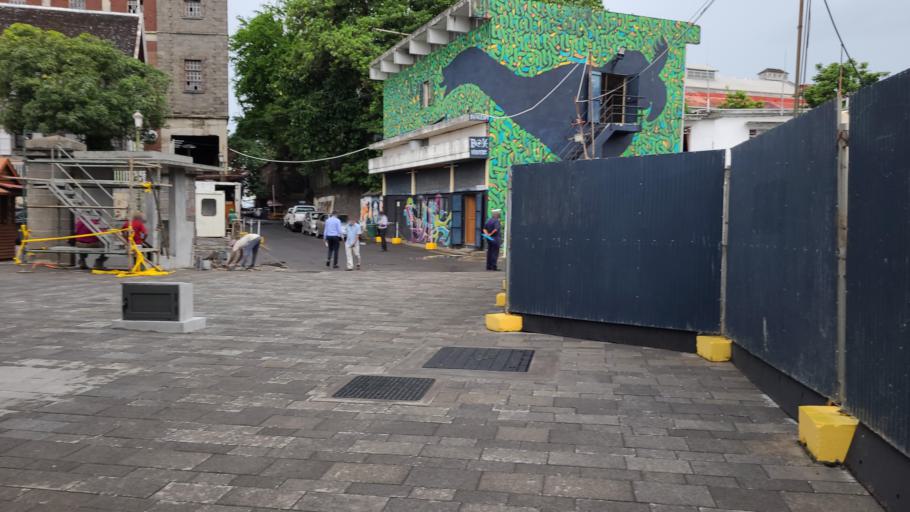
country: MU
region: Port Louis
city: Port Louis
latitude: -20.1599
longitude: 57.5012
